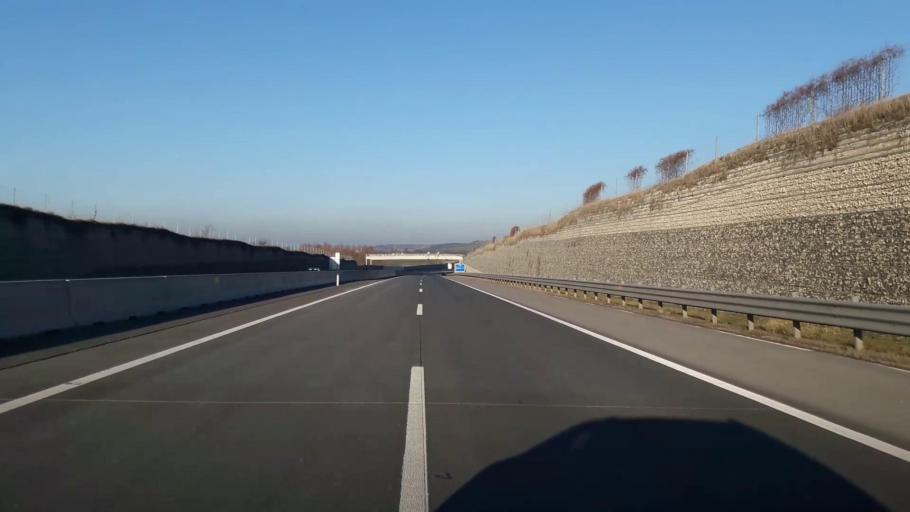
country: AT
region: Lower Austria
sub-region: Politischer Bezirk Mistelbach
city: Wolkersdorf im Weinviertel
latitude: 48.3806
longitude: 16.4911
